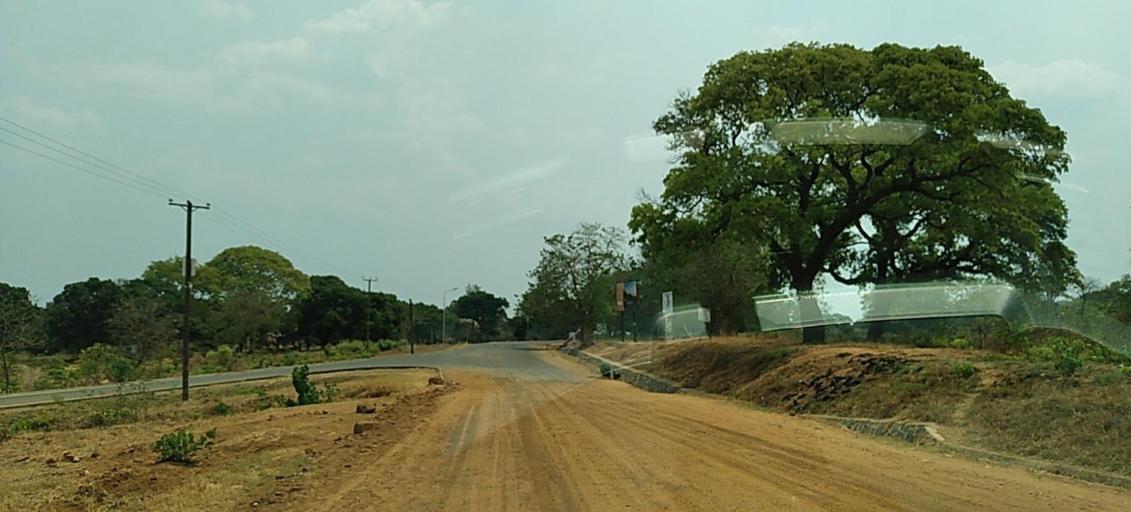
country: ZM
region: North-Western
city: Zambezi
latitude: -13.5490
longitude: 23.1065
